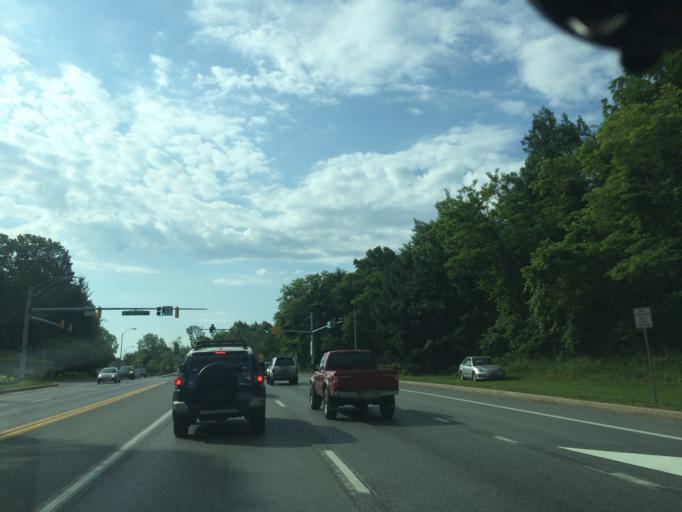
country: US
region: Maryland
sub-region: Baltimore County
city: Reisterstown
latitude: 39.4821
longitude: -76.8573
